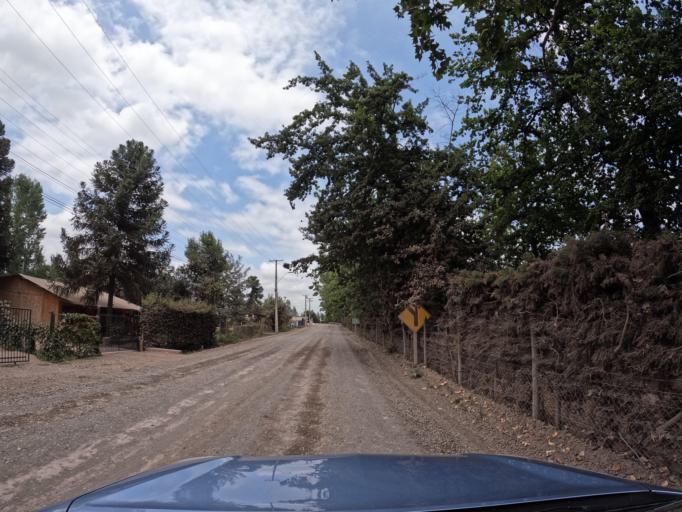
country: CL
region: O'Higgins
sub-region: Provincia de Colchagua
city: Chimbarongo
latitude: -34.7394
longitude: -70.9774
